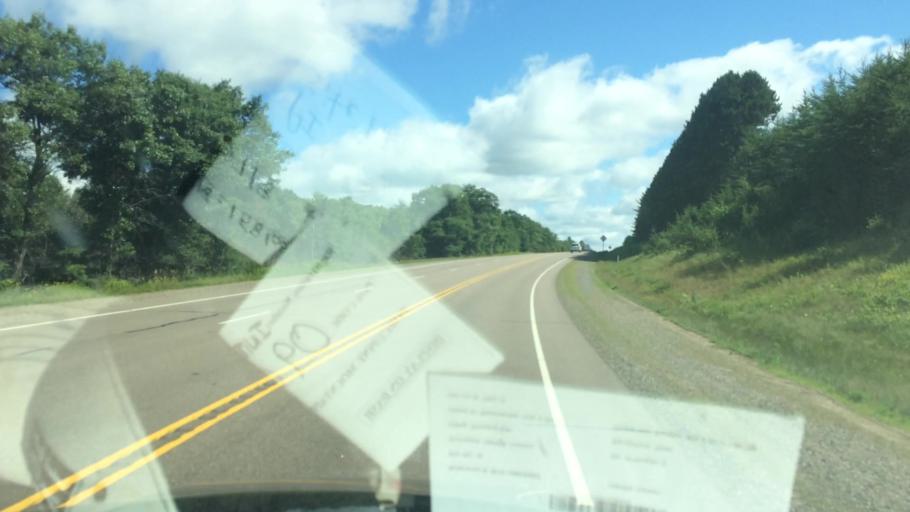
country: US
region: Wisconsin
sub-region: Oneida County
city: Rhinelander
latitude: 45.5922
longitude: -89.5684
